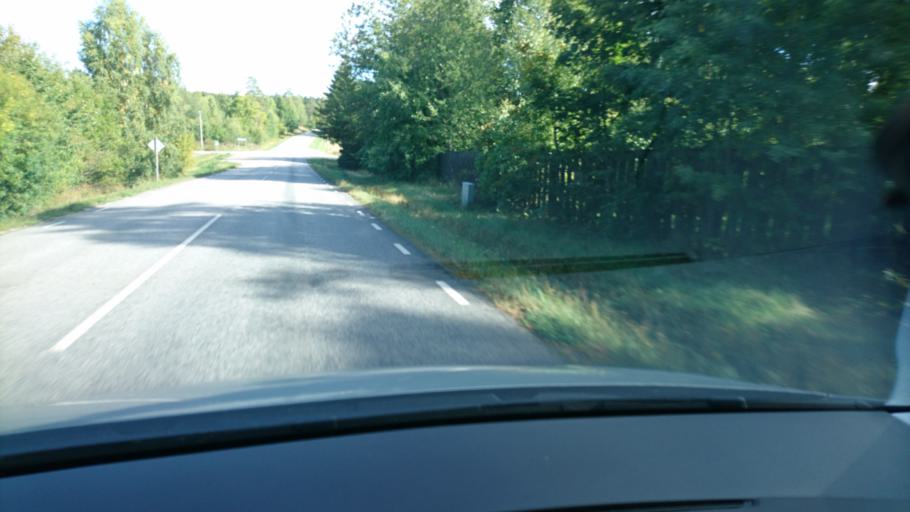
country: SE
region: Soedermanland
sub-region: Strangnas Kommun
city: Stallarholmen
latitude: 59.3444
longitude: 17.1235
